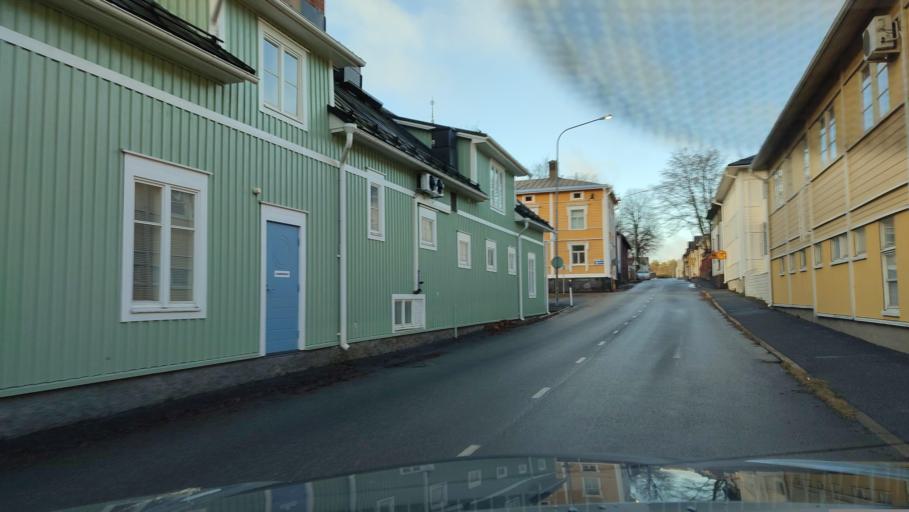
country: FI
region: Ostrobothnia
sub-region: Sydosterbotten
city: Kristinestad
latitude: 62.2727
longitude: 21.3792
